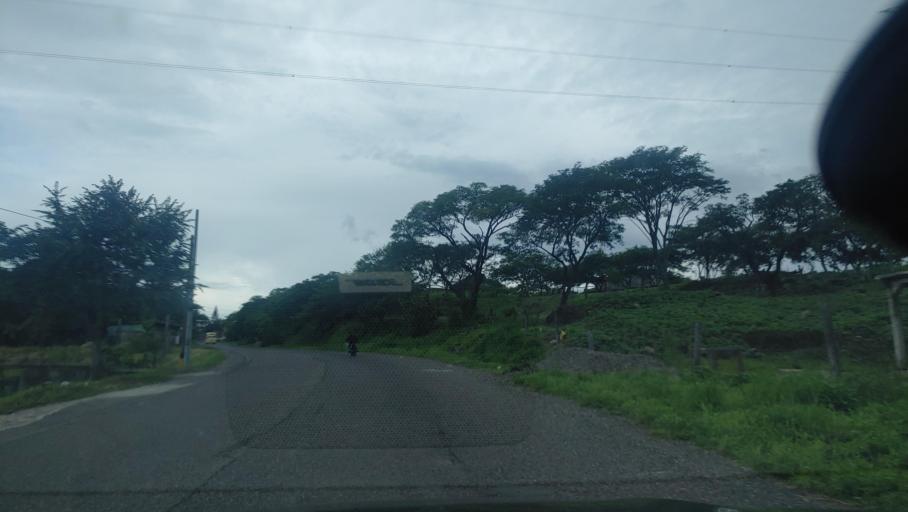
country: HN
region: Choluteca
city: Corpus
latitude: 13.3629
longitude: -86.9910
